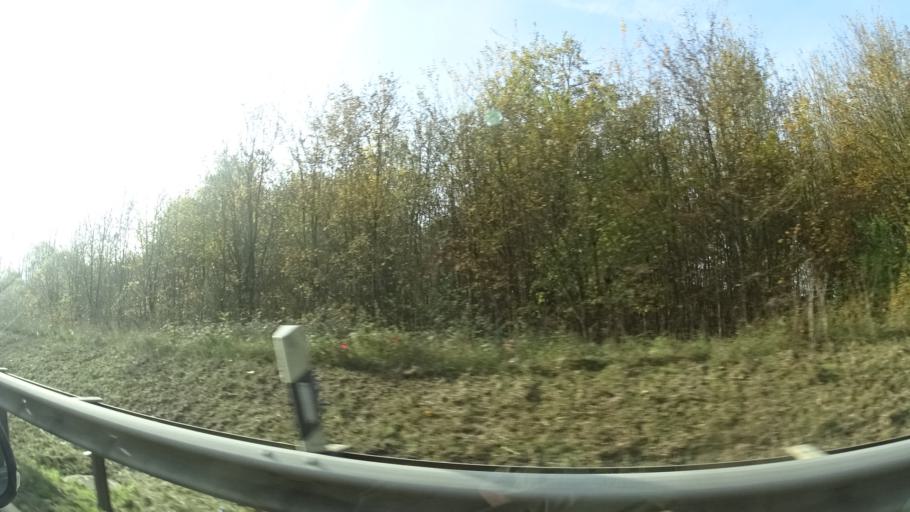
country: DE
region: Baden-Wuerttemberg
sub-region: Karlsruhe Region
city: Fahrenbach
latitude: 49.3930
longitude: 9.1986
